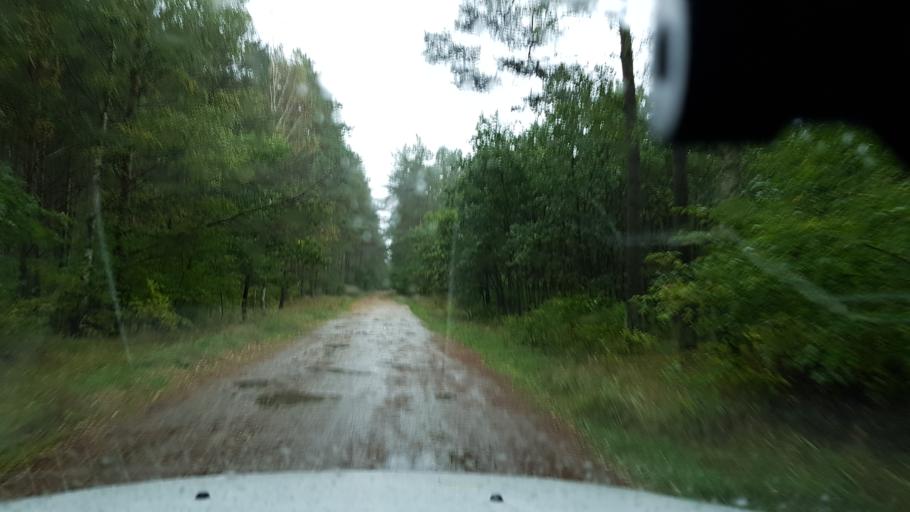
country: PL
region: West Pomeranian Voivodeship
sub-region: Powiat goleniowski
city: Przybiernow
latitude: 53.7361
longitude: 14.8012
